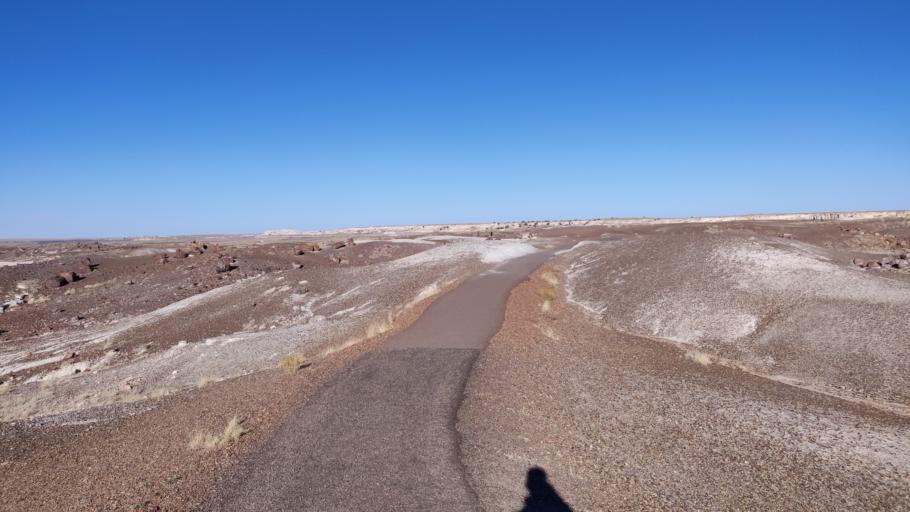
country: US
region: Arizona
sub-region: Navajo County
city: Holbrook
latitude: 34.8640
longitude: -109.7898
